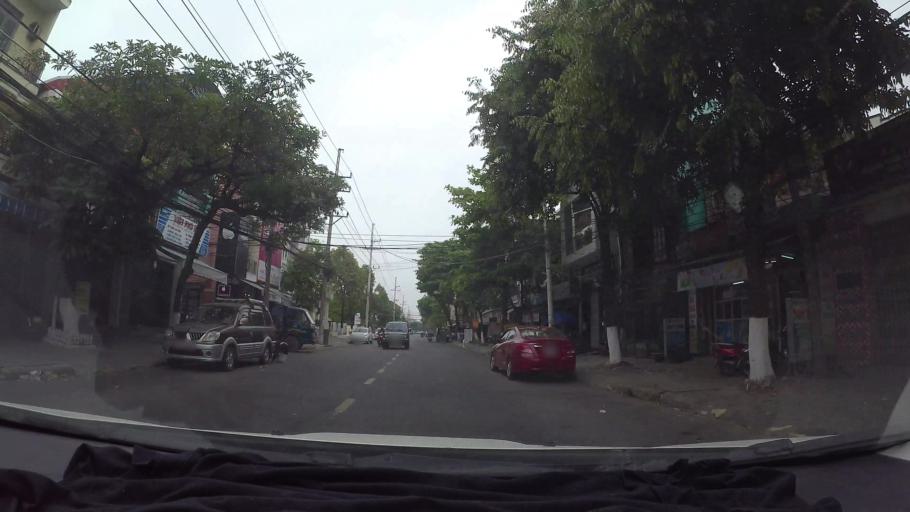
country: VN
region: Da Nang
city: Da Nang
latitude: 16.0506
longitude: 108.2132
